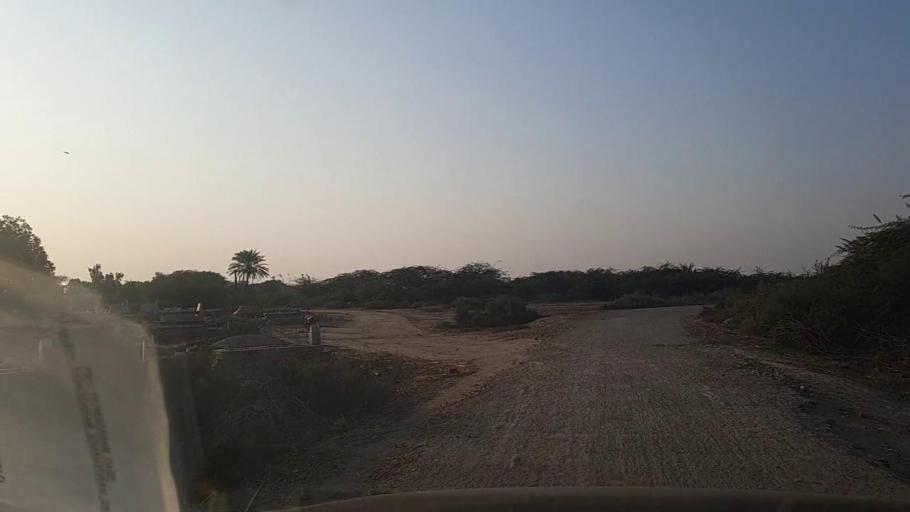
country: PK
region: Sindh
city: Keti Bandar
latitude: 24.3084
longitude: 67.6024
